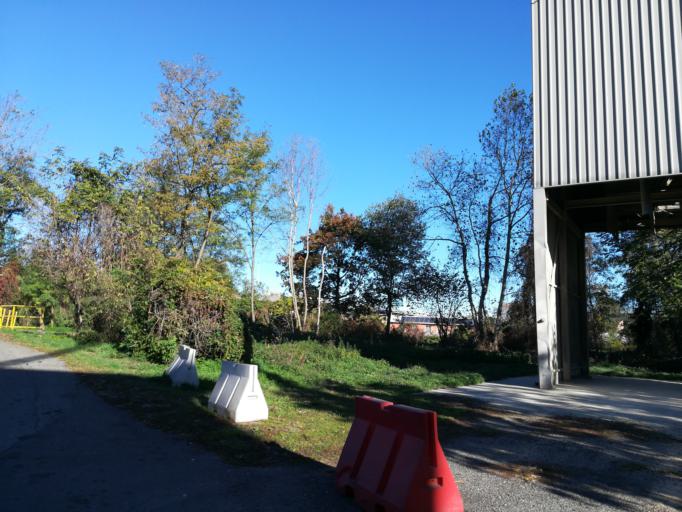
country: IT
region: Lombardy
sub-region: Citta metropolitana di Milano
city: Novegro-Tregarezzo-San Felice
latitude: 45.4681
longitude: 9.2534
